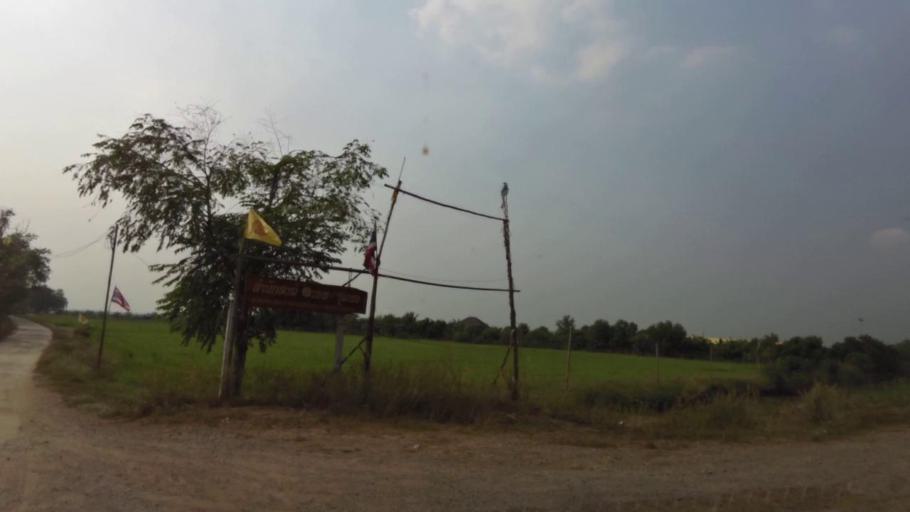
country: TH
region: Phra Nakhon Si Ayutthaya
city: Phra Nakhon Si Ayutthaya
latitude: 14.3153
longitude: 100.5610
